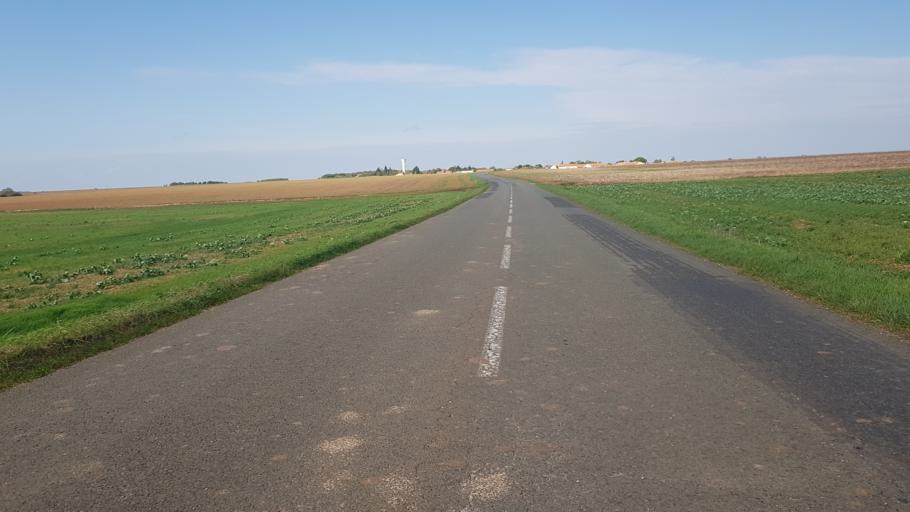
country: FR
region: Poitou-Charentes
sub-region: Departement de la Vienne
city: Chasseneuil-du-Poitou
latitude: 46.6524
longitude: 0.3439
